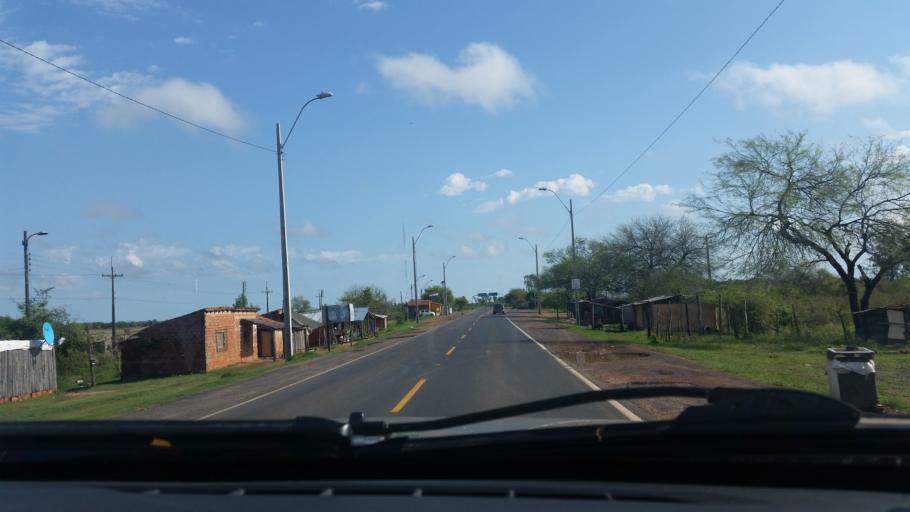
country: PY
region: Presidente Hayes
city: Benjamin Aceval
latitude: -24.9459
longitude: -57.5527
